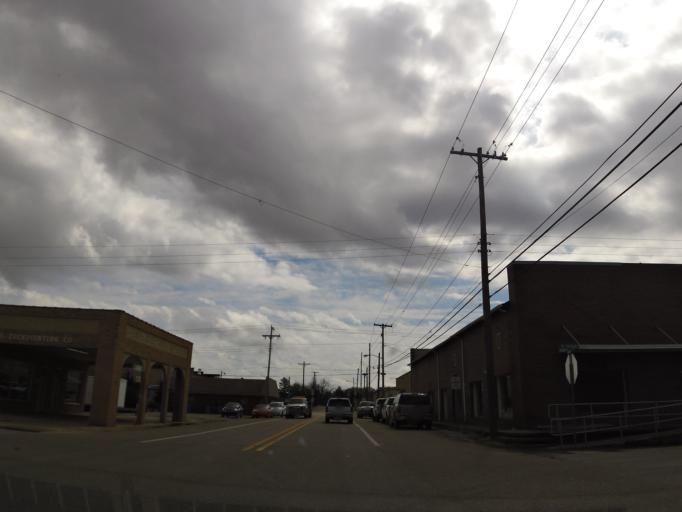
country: US
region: Arkansas
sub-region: Clay County
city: Corning
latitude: 36.4085
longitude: -90.5813
